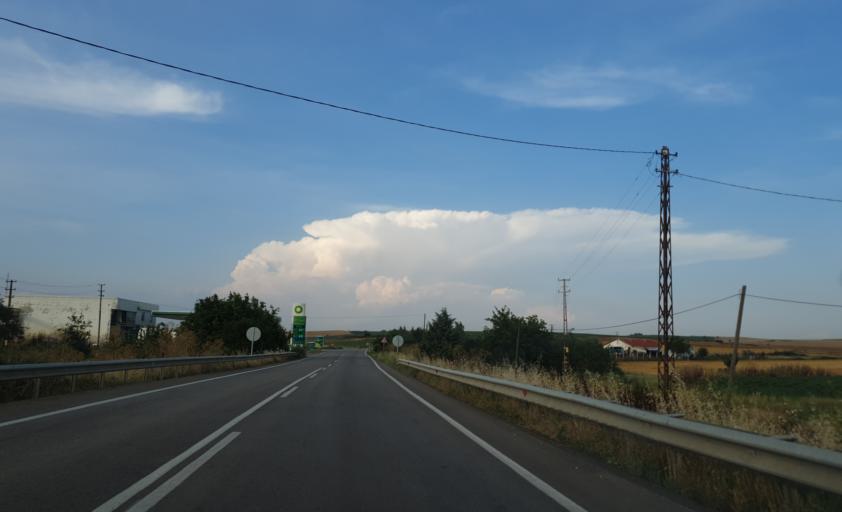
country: TR
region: Tekirdag
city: Hayrabolu
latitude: 41.2333
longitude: 27.1256
